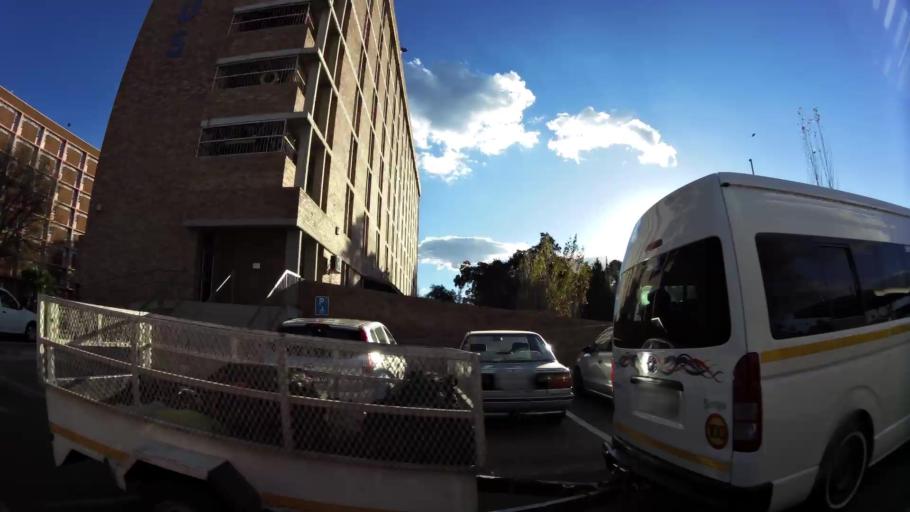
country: ZA
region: North-West
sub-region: Dr Kenneth Kaunda District Municipality
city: Potchefstroom
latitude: -26.6968
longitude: 27.0885
